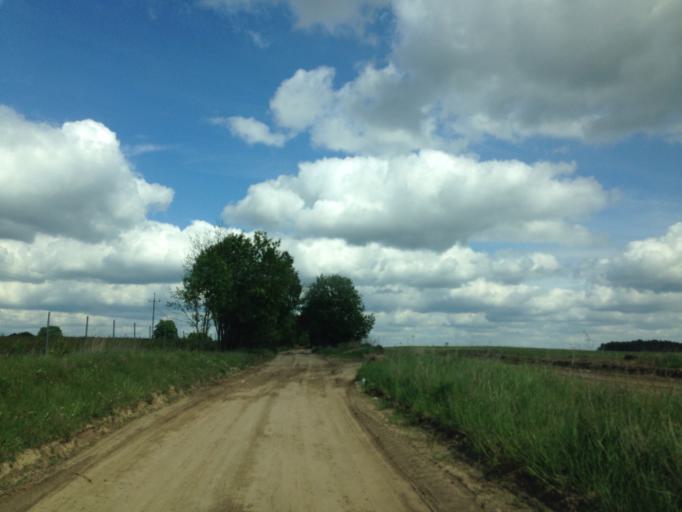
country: PL
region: Warmian-Masurian Voivodeship
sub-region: Powiat nidzicki
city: Kozlowo
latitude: 53.4394
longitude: 20.3083
